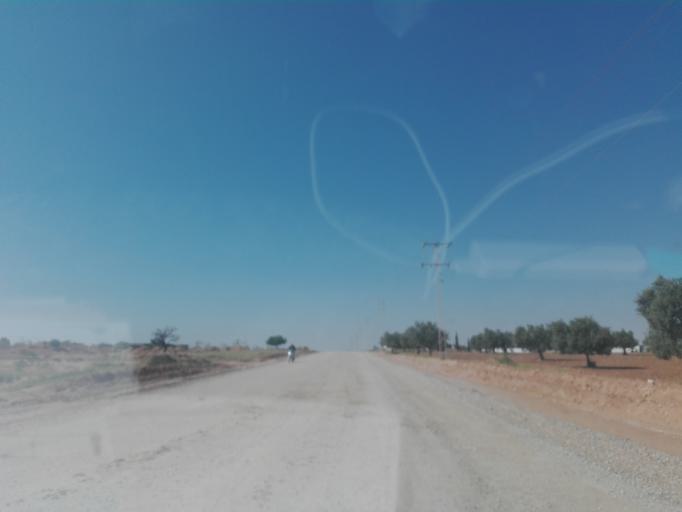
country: TN
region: Safaqis
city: Sfax
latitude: 34.7235
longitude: 10.5109
